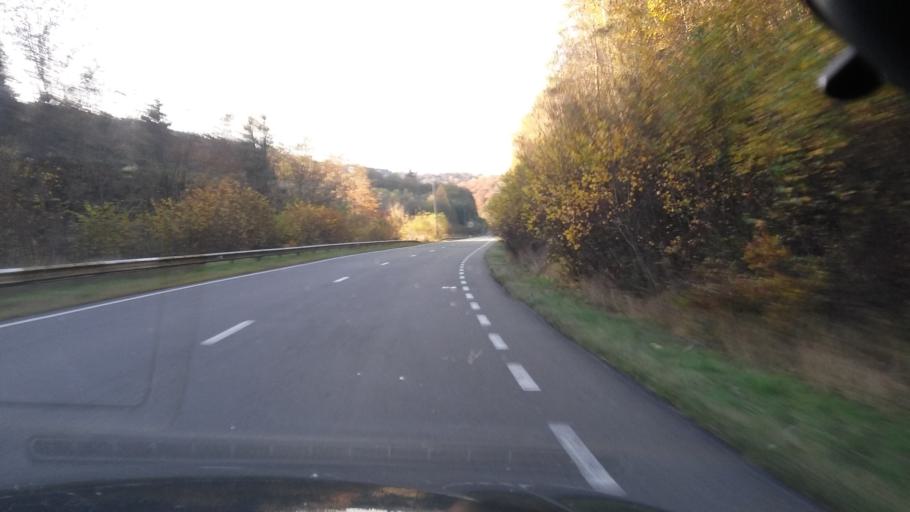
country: BE
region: Wallonia
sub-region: Province du Luxembourg
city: Bouillon
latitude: 49.7653
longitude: 5.0907
